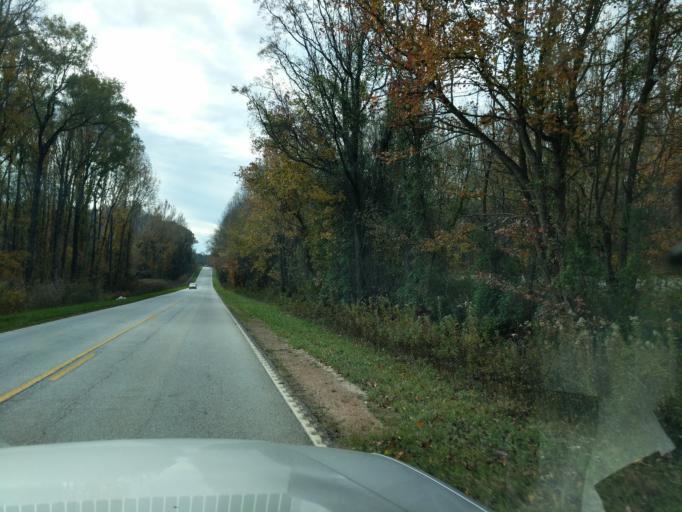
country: US
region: South Carolina
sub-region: Laurens County
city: Watts Mills
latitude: 34.5691
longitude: -82.0040
